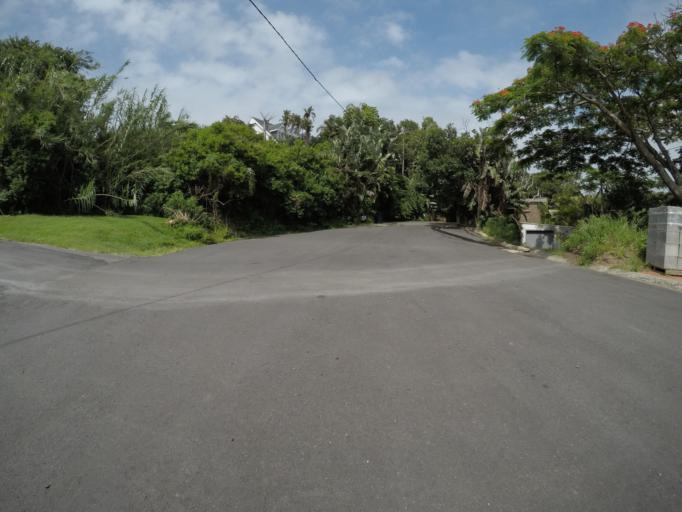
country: ZA
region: Eastern Cape
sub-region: Buffalo City Metropolitan Municipality
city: East London
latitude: -32.9343
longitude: 28.0261
